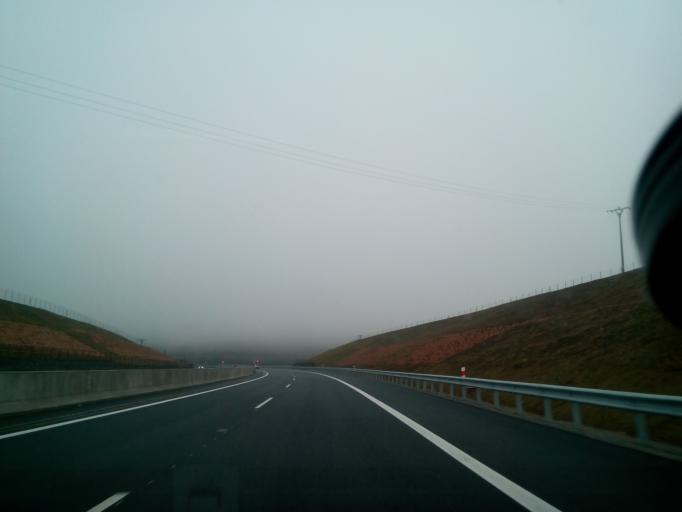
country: SK
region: Presovsky
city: Sabinov
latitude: 49.0021
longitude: 21.0571
